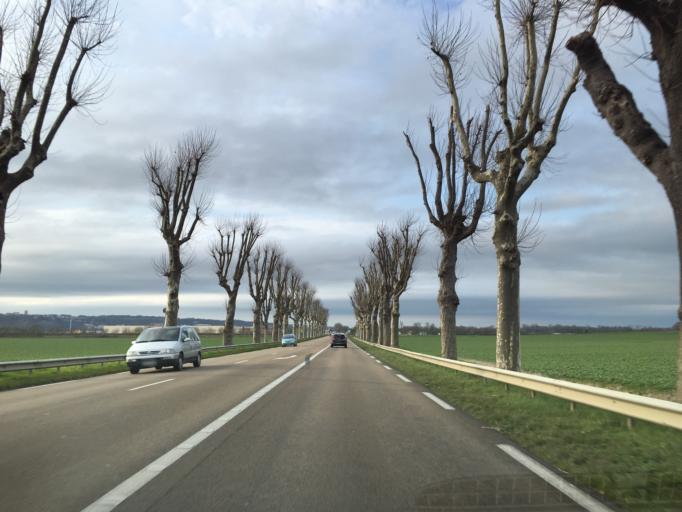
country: FR
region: Bourgogne
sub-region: Departement de l'Yonne
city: Maillot
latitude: 48.1661
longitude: 3.2991
